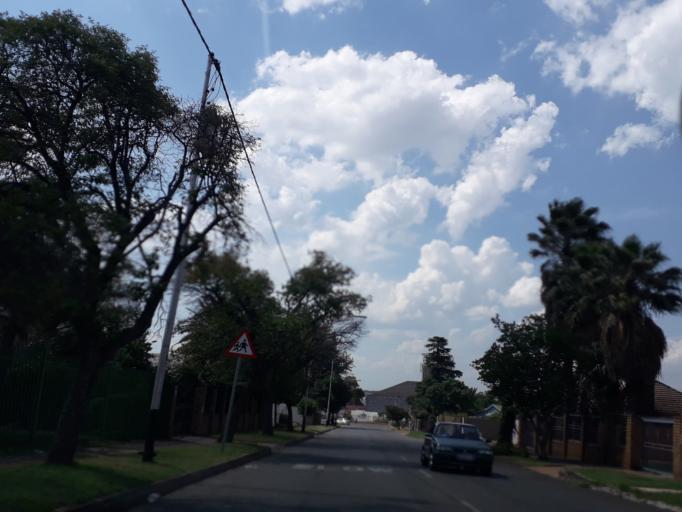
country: ZA
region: Gauteng
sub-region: City of Johannesburg Metropolitan Municipality
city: Johannesburg
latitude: -26.2419
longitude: 28.0204
